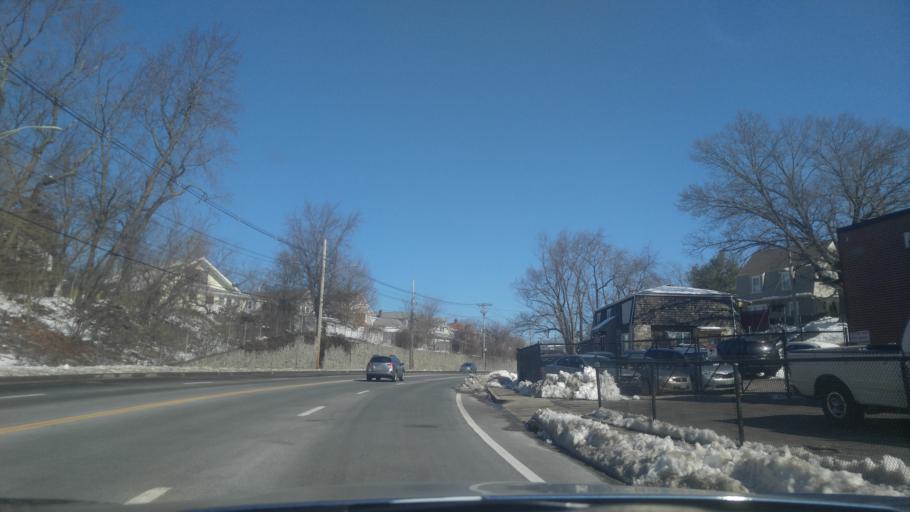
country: US
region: Rhode Island
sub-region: Providence County
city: Cranston
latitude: 41.7711
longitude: -71.4053
